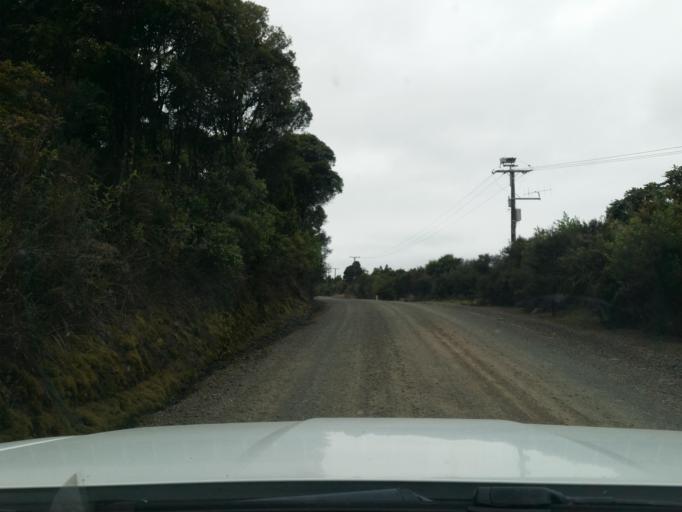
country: NZ
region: Northland
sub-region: Kaipara District
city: Dargaville
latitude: -35.7192
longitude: 173.6458
